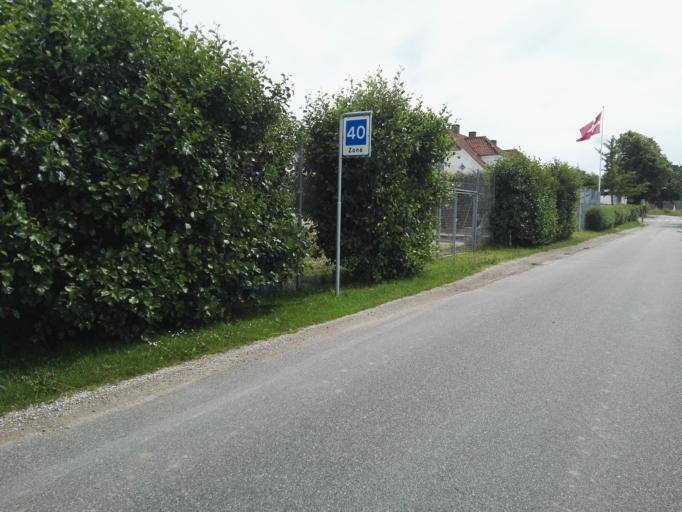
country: DK
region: Capital Region
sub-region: Hillerod Kommune
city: Skaevinge
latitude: 55.8850
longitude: 12.1303
